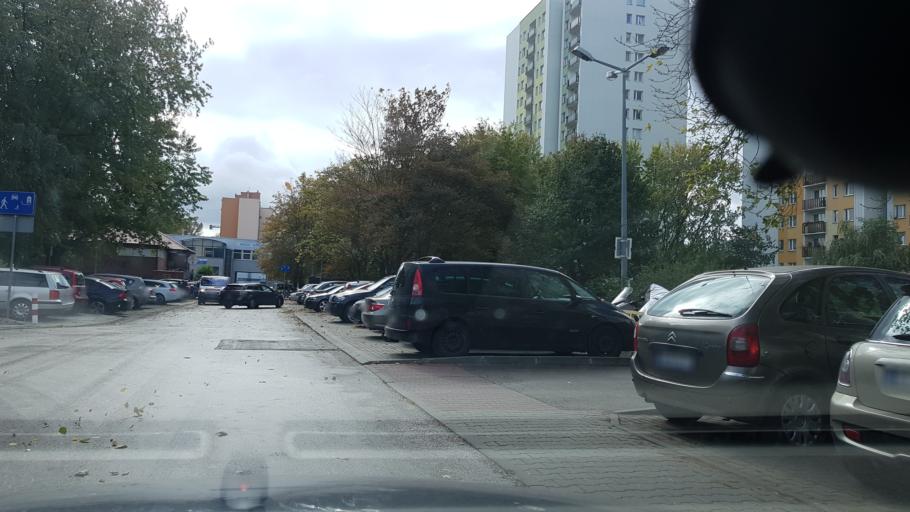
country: PL
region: Masovian Voivodeship
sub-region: Warszawa
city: Bielany
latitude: 52.2748
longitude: 20.9308
